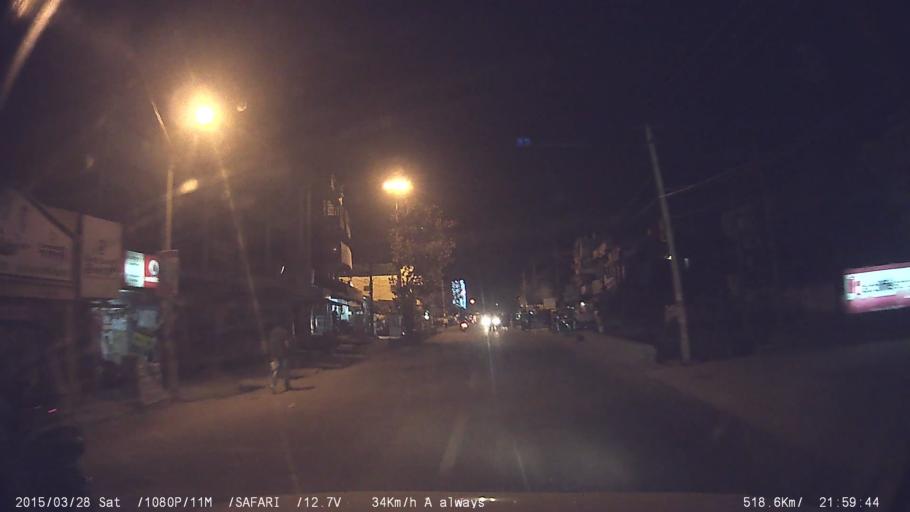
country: IN
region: Karnataka
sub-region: Bangalore Urban
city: Bangalore
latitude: 12.8566
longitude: 77.5889
